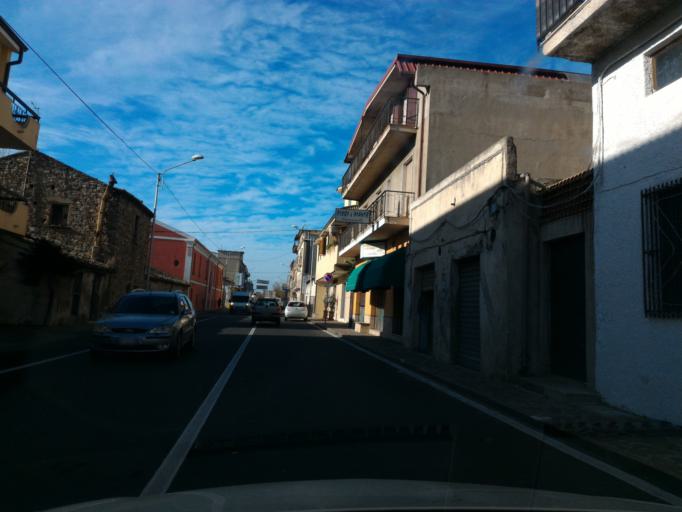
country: IT
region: Calabria
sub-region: Provincia di Catanzaro
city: Botricello
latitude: 38.9366
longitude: 16.8627
